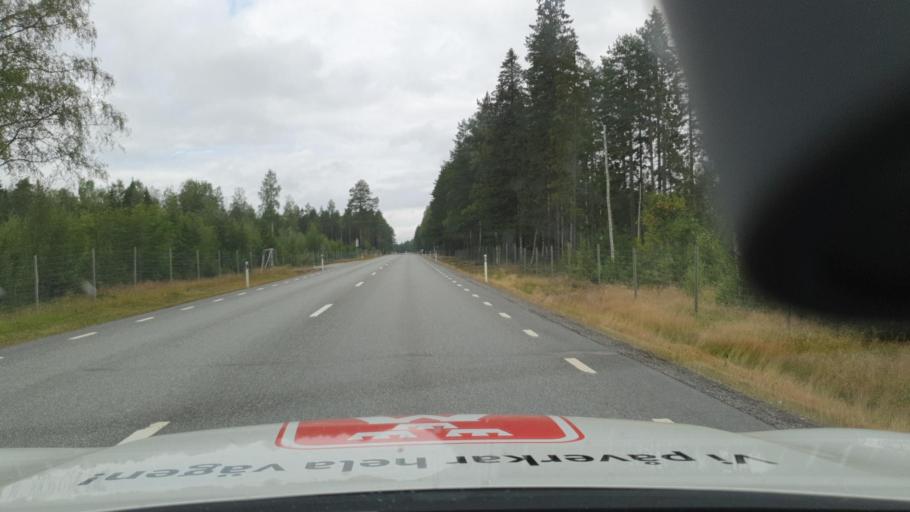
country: SE
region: Vaesterbotten
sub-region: Skelleftea Kommun
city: Burea
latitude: 64.5460
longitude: 21.2503
